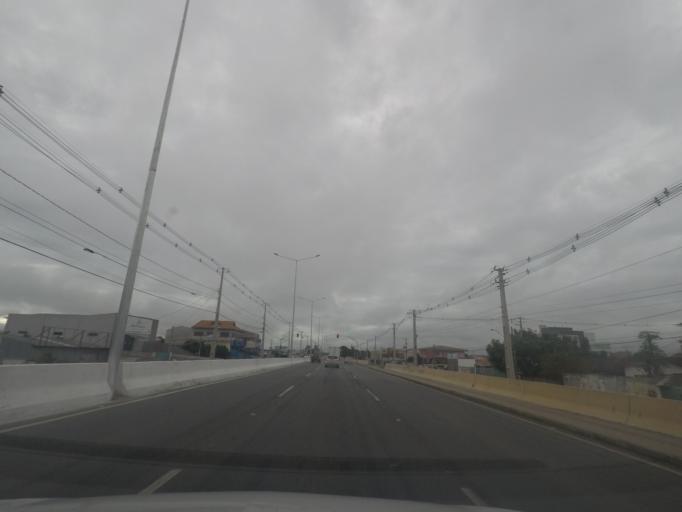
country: BR
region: Parana
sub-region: Pinhais
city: Pinhais
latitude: -25.4396
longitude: -49.1577
